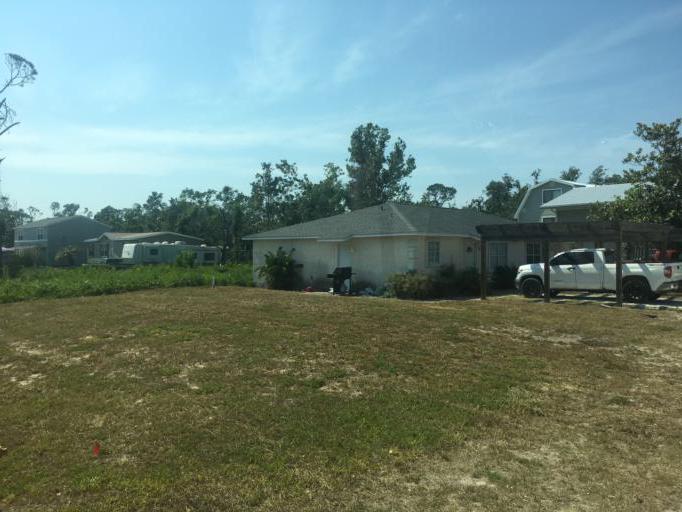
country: US
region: Florida
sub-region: Bay County
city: Upper Grand Lagoon
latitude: 30.1573
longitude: -85.7265
